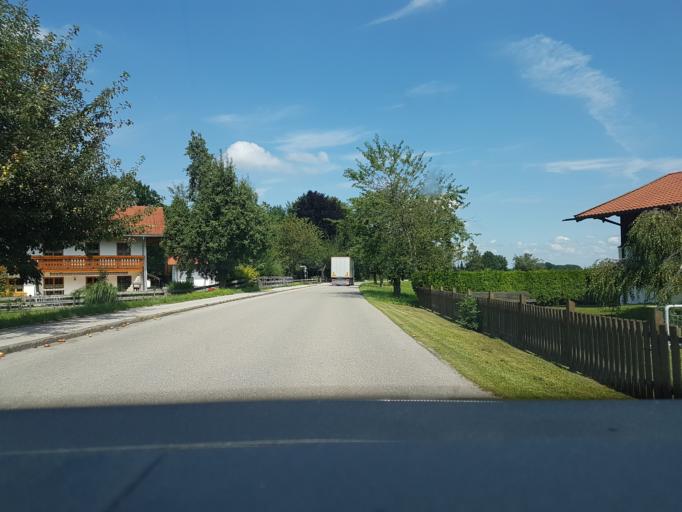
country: DE
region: Bavaria
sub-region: Upper Bavaria
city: Brannenburg
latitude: 47.7683
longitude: 12.0817
